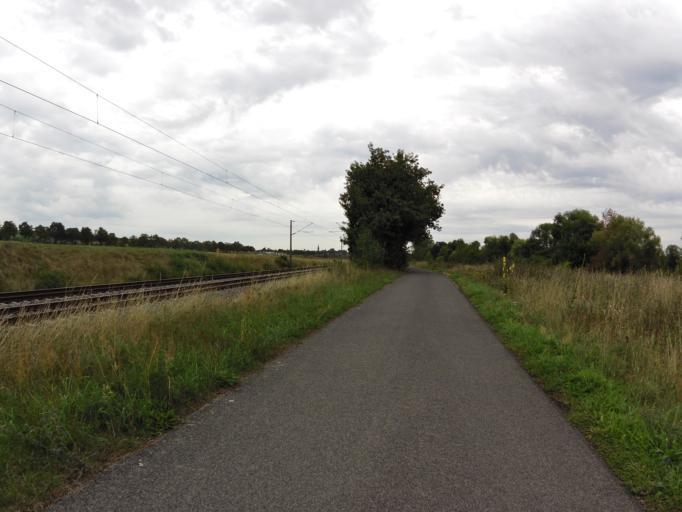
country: DE
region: Bavaria
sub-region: Regierungsbezirk Unterfranken
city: Wonfurt
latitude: 50.0150
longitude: 10.4244
